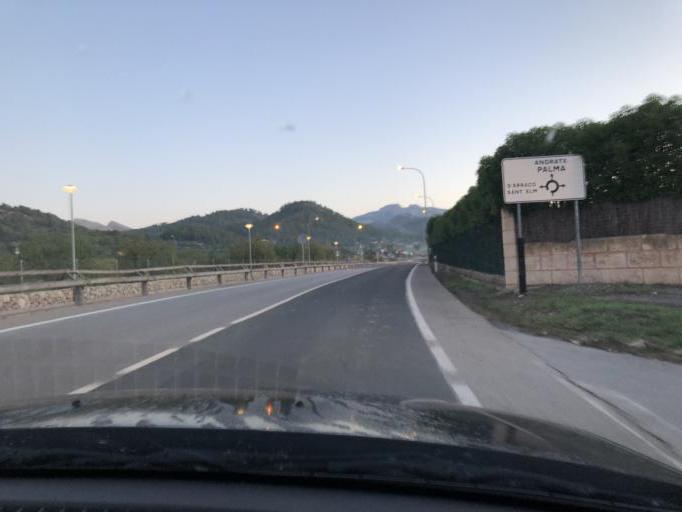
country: ES
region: Balearic Islands
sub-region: Illes Balears
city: Andratx
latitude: 39.5589
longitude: 2.3998
